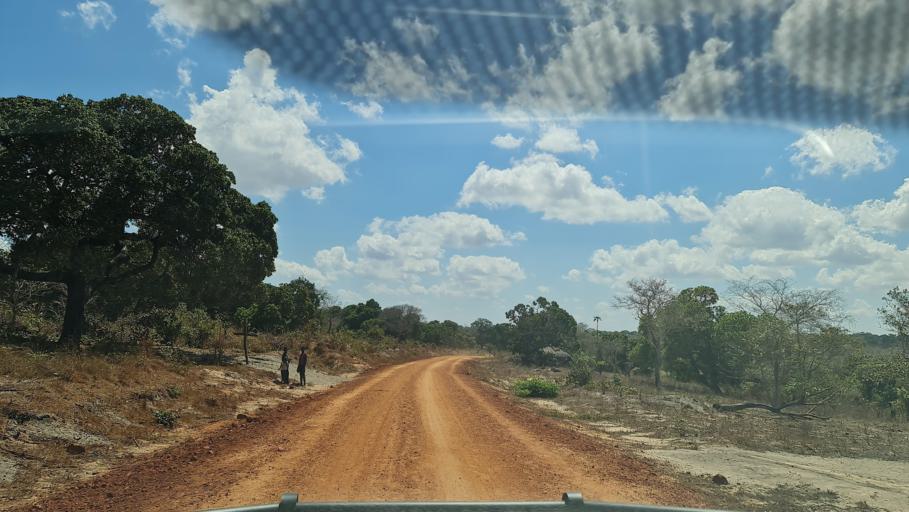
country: MZ
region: Nampula
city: Nacala
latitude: -14.1702
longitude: 40.2466
